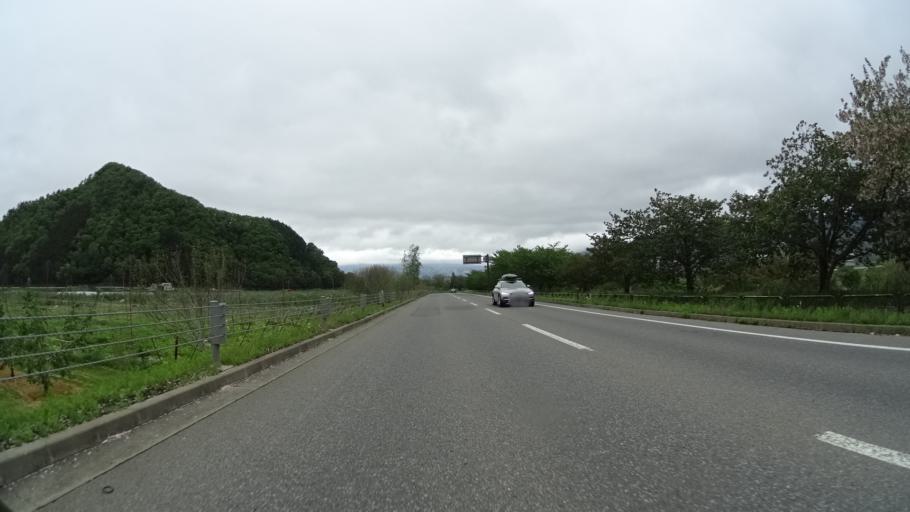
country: JP
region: Nagano
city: Nakano
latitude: 36.7495
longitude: 138.3995
